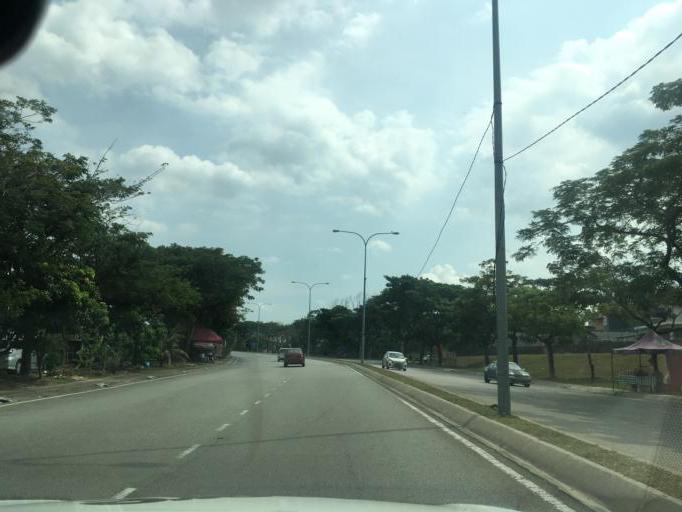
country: MY
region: Selangor
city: Shah Alam
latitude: 3.0812
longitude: 101.4811
